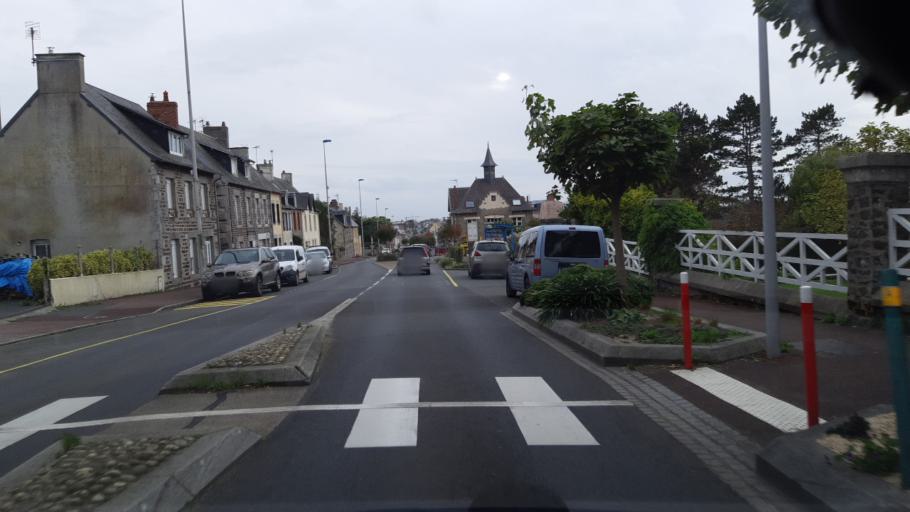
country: FR
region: Lower Normandy
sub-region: Departement de la Manche
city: Donville-les-Bains
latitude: 48.8502
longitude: -1.5733
